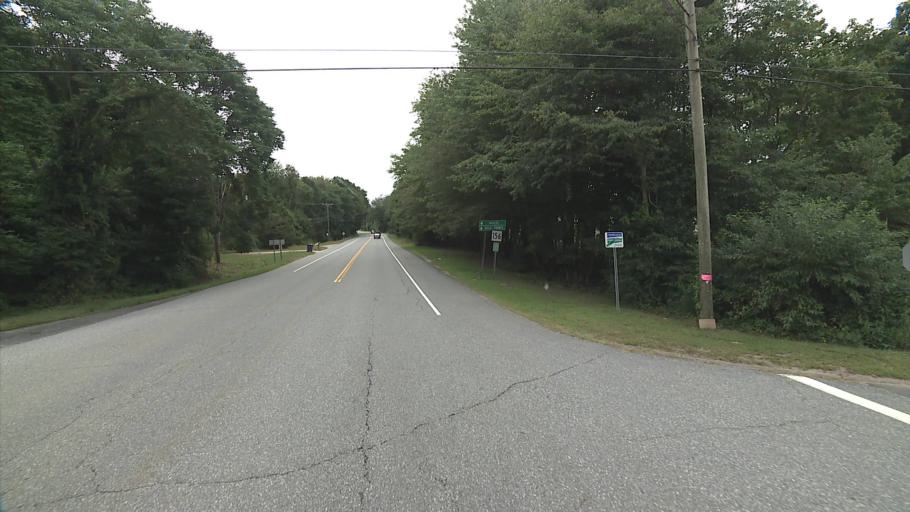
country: US
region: Connecticut
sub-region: Middlesex County
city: Old Saybrook Center
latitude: 41.3017
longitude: -72.3272
